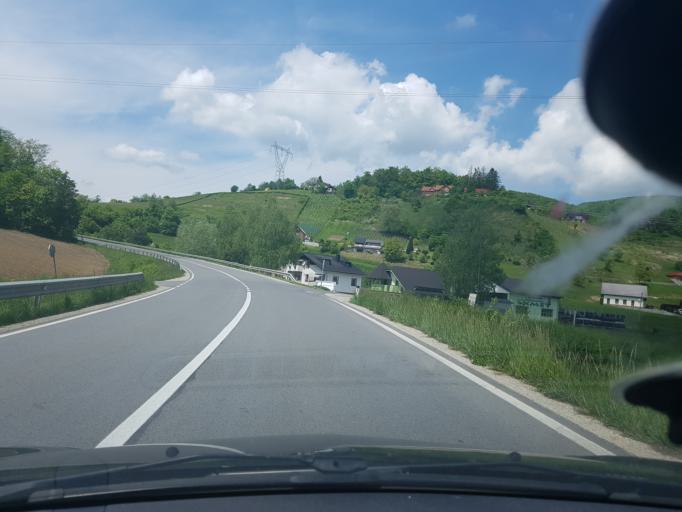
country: SI
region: Rogaska Slatina
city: Rogaska Slatina
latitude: 46.2510
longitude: 15.6373
